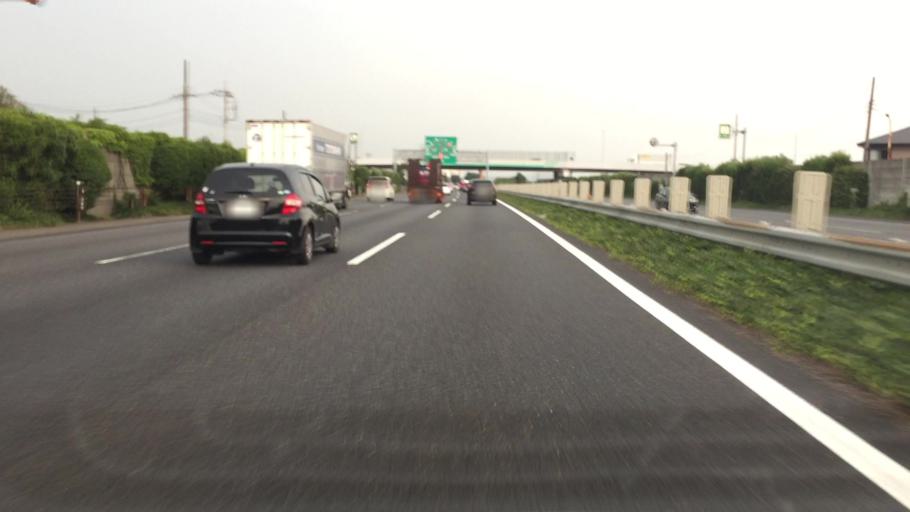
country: JP
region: Saitama
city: Kukichuo
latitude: 36.0756
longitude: 139.6432
